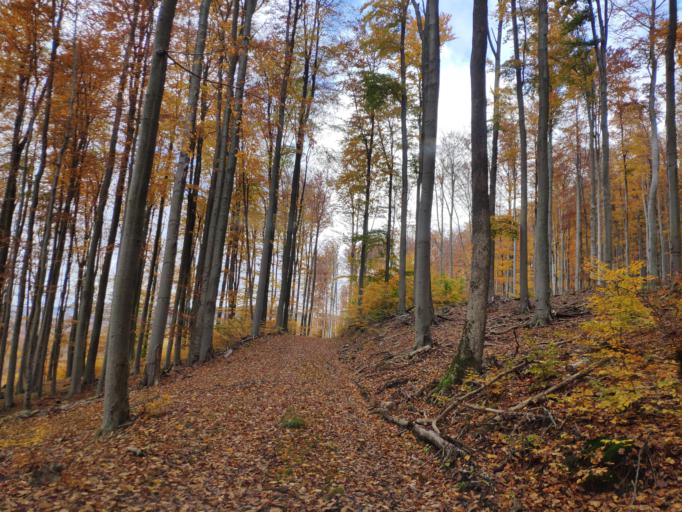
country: SK
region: Kosicky
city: Medzev
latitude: 48.7335
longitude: 20.9957
